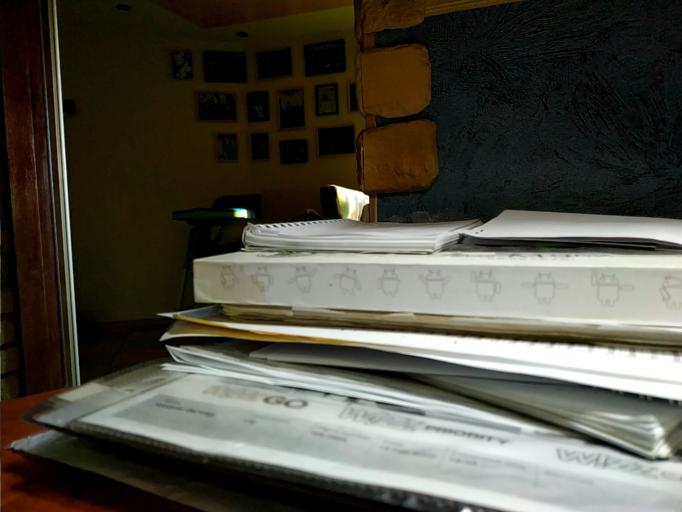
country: RU
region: Novgorod
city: Kholm
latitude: 57.0897
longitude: 31.5171
